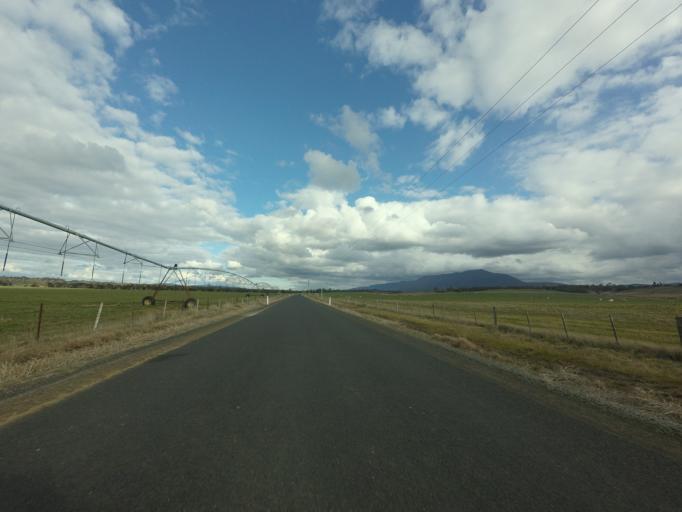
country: AU
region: Tasmania
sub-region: Northern Midlands
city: Longford
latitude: -41.8228
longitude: 147.2032
